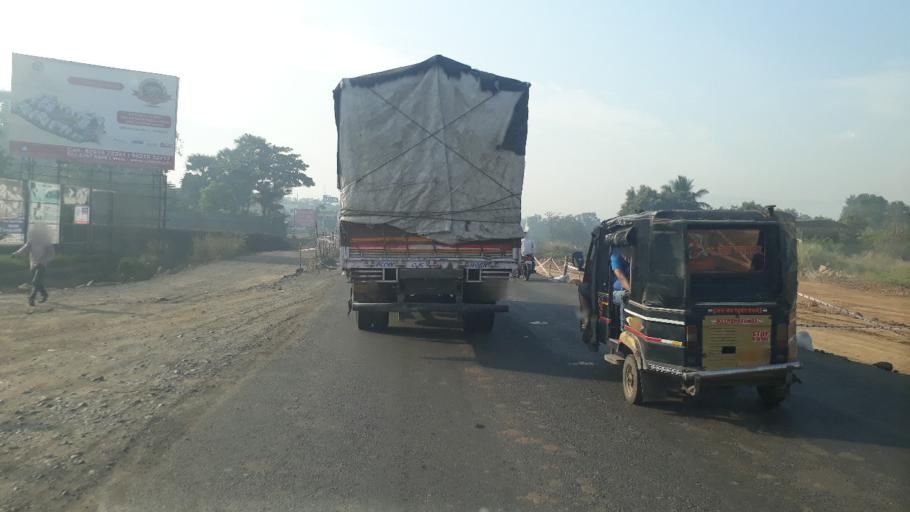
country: IN
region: Maharashtra
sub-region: Raigarh
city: Kalundri
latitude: 18.9301
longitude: 73.1272
